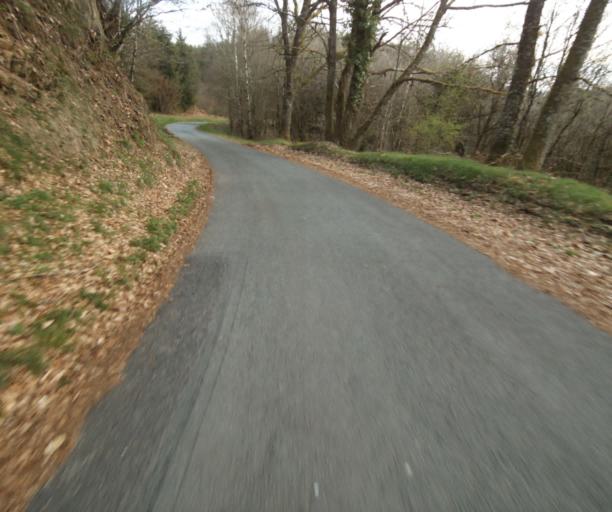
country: FR
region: Limousin
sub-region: Departement de la Correze
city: Correze
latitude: 45.3800
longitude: 1.8855
